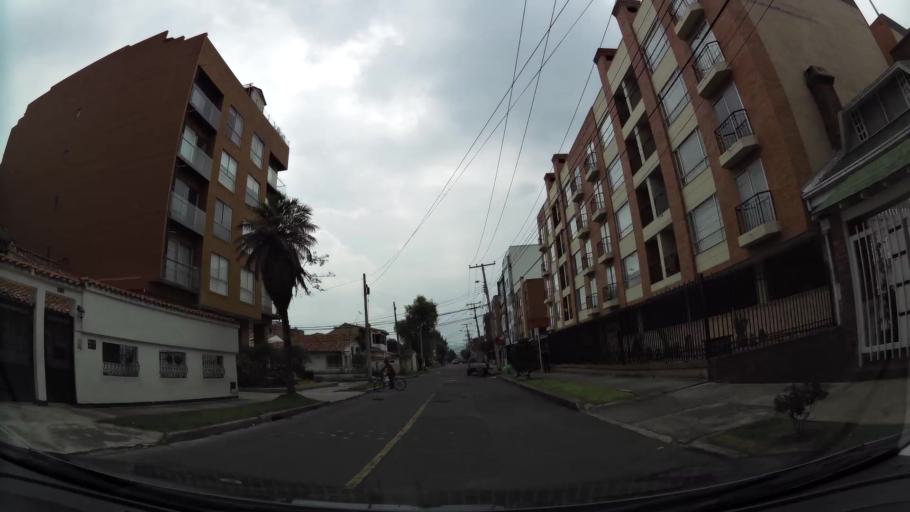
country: CO
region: Bogota D.C.
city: Barrio San Luis
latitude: 4.7257
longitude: -74.0417
